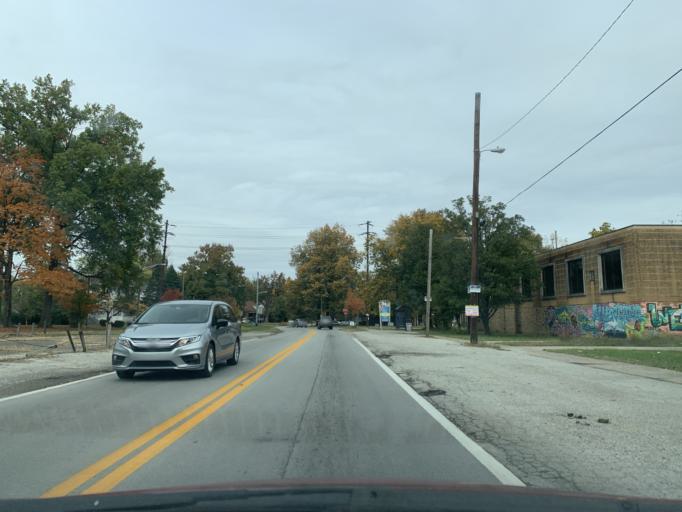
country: US
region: Kentucky
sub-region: Jefferson County
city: Audubon Park
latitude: 38.1785
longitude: -85.7647
